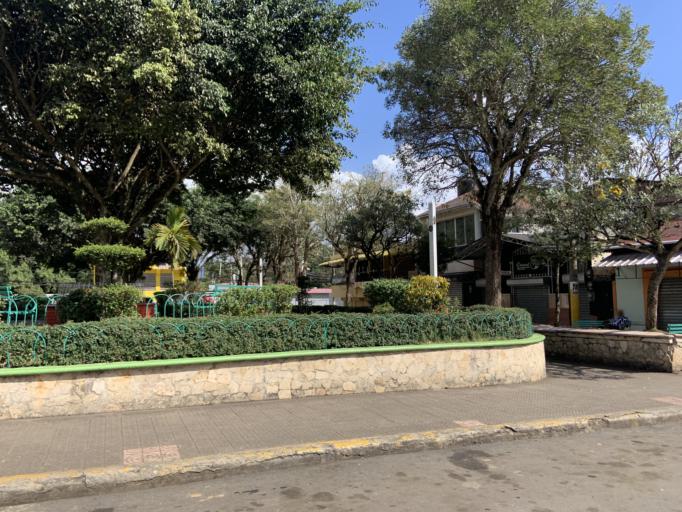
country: DO
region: Monte Plata
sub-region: Yamasa
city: Yamasa
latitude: 18.7696
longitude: -70.0251
